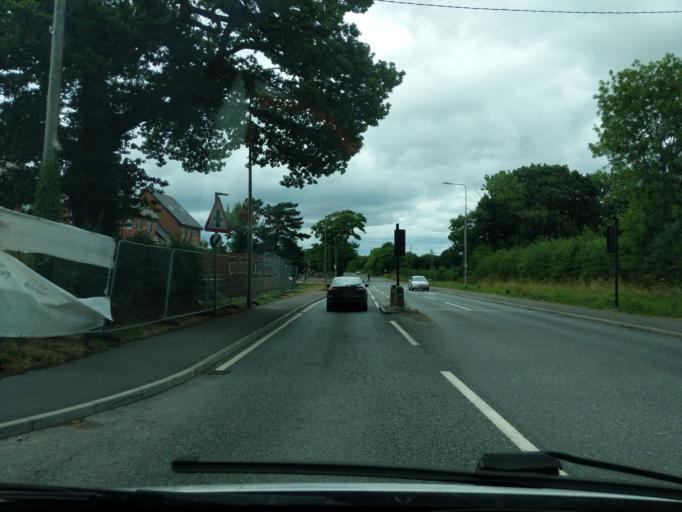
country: GB
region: England
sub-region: Cheshire West and Chester
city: Cuddington
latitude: 53.2473
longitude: -2.5974
